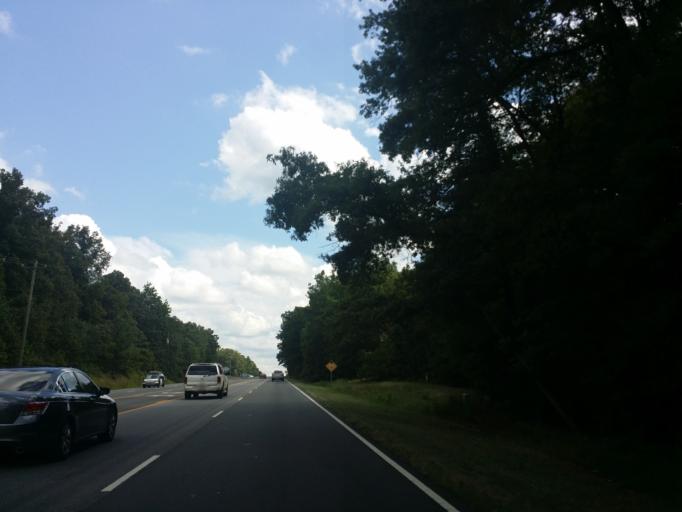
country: US
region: North Carolina
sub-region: Durham County
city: Durham
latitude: 35.9611
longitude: -78.8444
